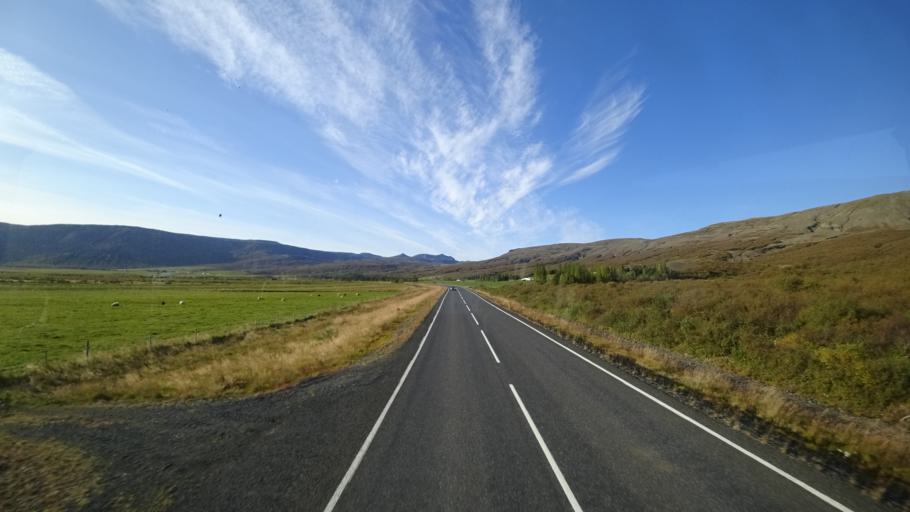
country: IS
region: South
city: Selfoss
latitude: 64.2324
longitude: -20.6351
